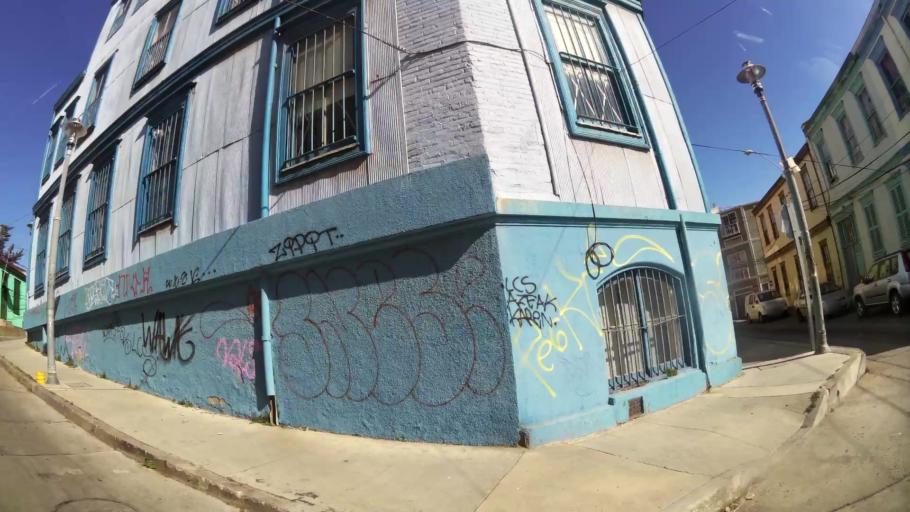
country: CL
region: Valparaiso
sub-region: Provincia de Valparaiso
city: Valparaiso
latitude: -33.0445
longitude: -71.6300
